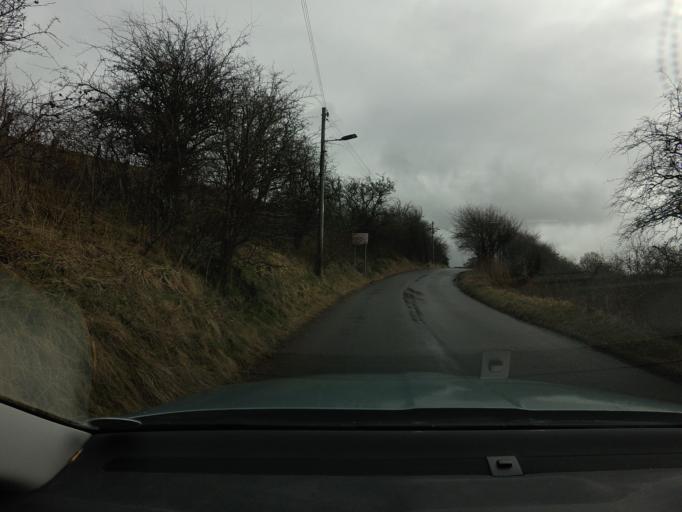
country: GB
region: Scotland
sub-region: South Lanarkshire
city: Lanark
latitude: 55.6042
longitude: -3.7873
